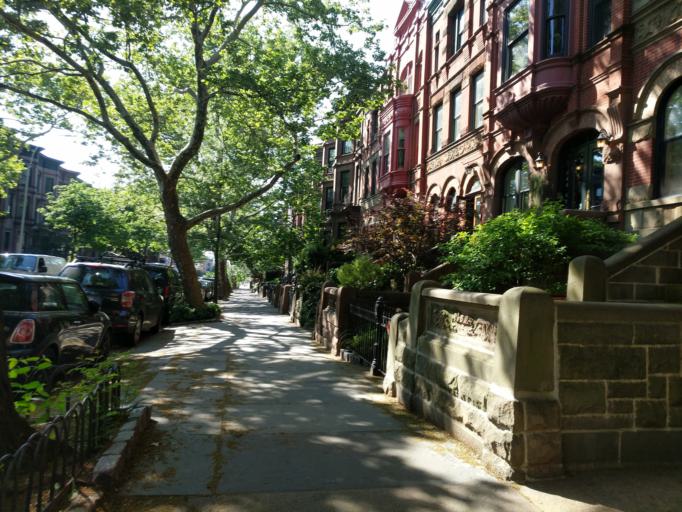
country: US
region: New York
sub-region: Kings County
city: Brooklyn
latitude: 40.6738
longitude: -73.9738
